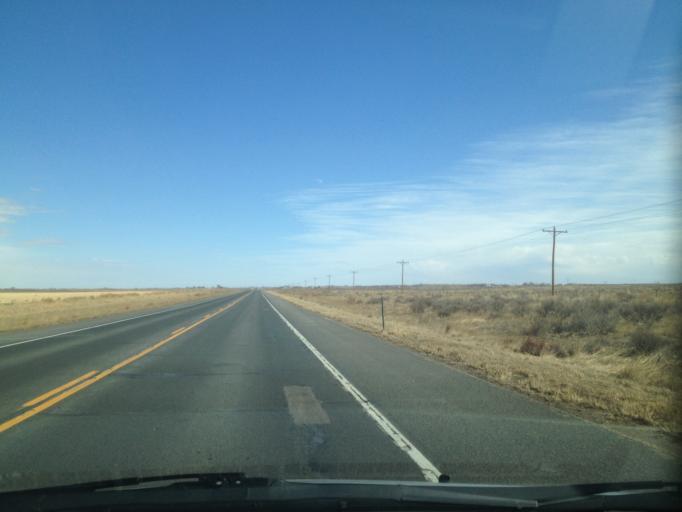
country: US
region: Colorado
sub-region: Weld County
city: Kersey
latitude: 40.2928
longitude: -104.2846
